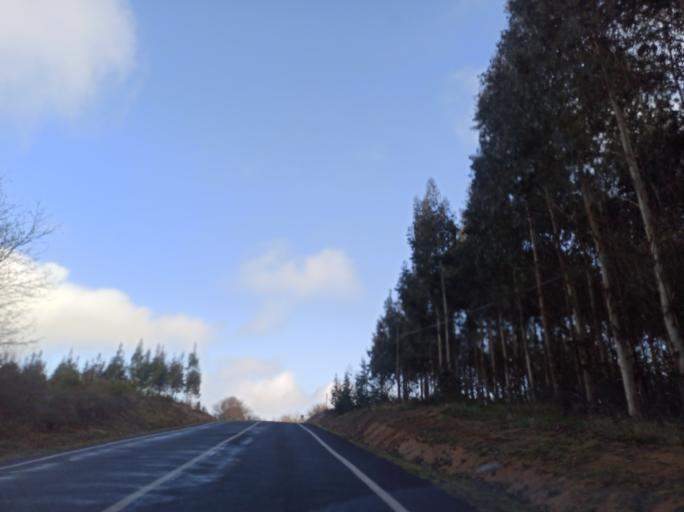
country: ES
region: Galicia
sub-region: Provincia da Coruna
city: Sobrado
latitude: 43.0819
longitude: -8.0036
